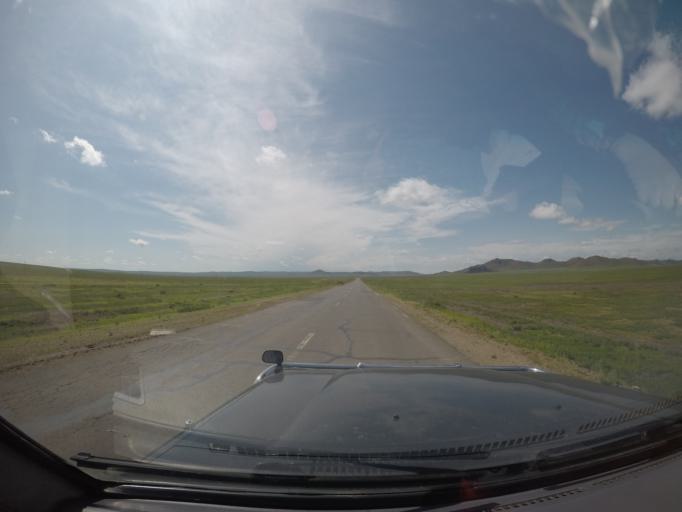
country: MN
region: Hentiy
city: Moron
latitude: 47.3806
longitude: 110.4378
